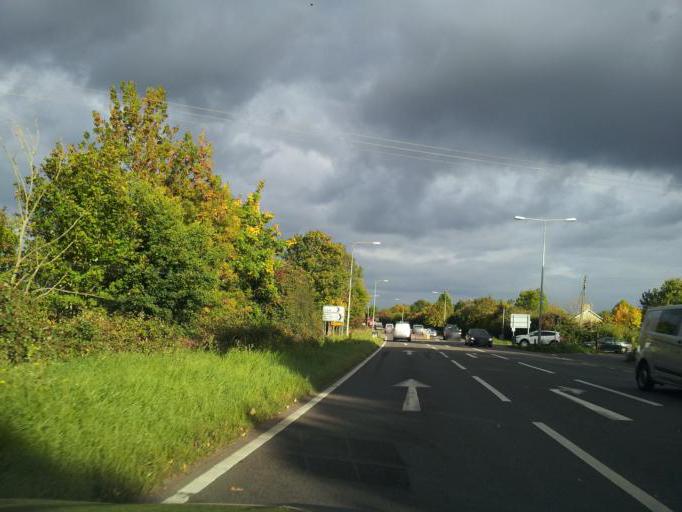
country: GB
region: England
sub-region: Cambridgeshire
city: Papworth Everard
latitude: 52.2219
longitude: -0.1485
